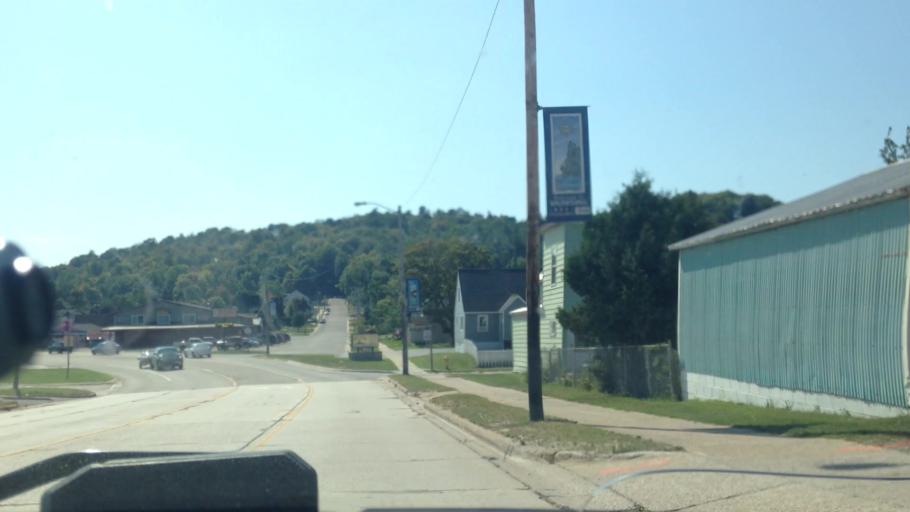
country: US
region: Michigan
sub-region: Alger County
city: Munising
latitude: 46.4085
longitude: -86.6508
